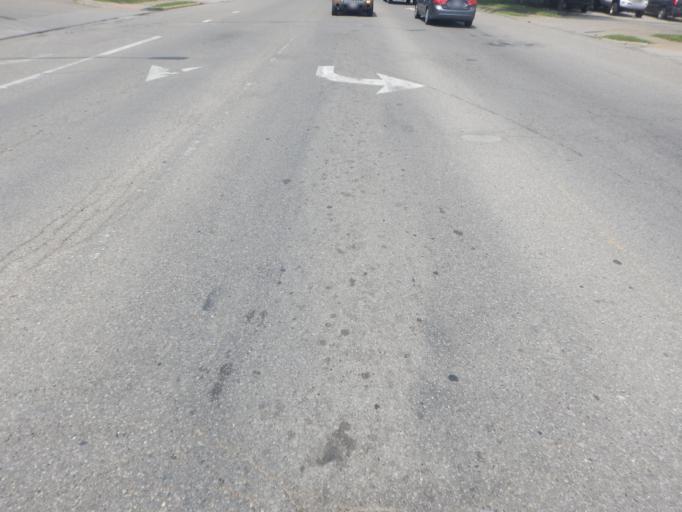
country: US
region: Ohio
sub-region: Muskingum County
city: Zanesville
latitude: 39.9539
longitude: -82.0062
